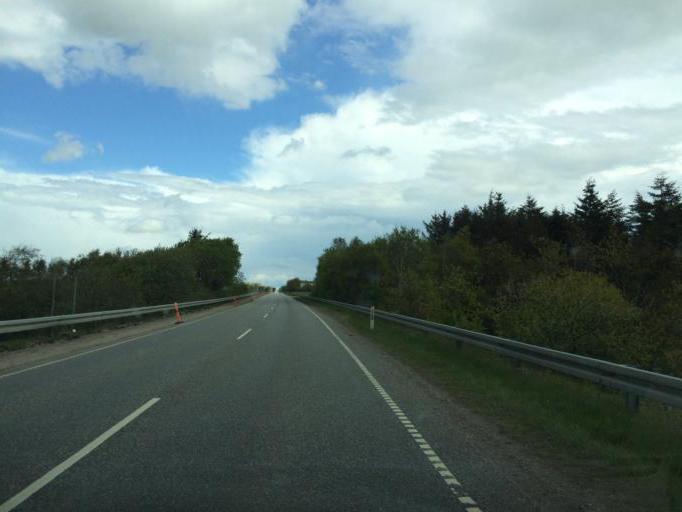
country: DK
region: North Denmark
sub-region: Vesthimmerland Kommune
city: Farso
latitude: 56.7164
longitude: 9.2745
